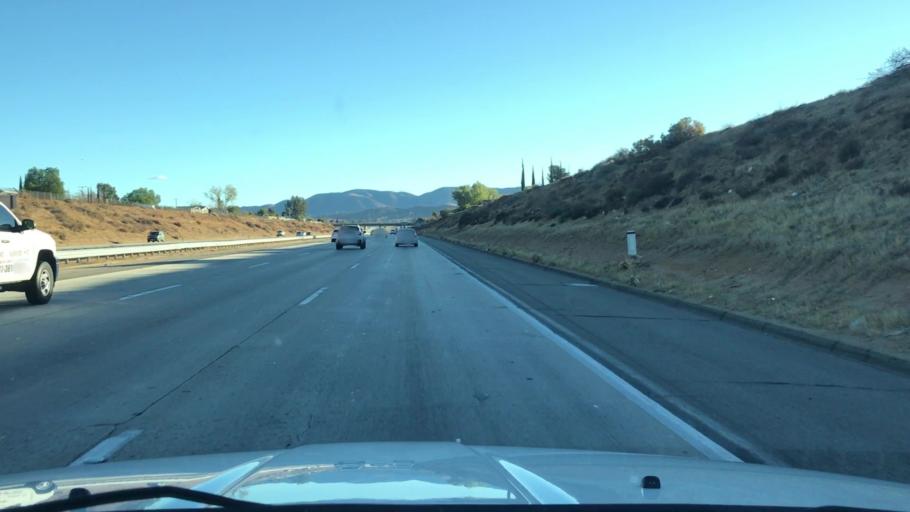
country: US
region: California
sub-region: Los Angeles County
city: Desert View Highlands
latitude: 34.6229
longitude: -118.1535
